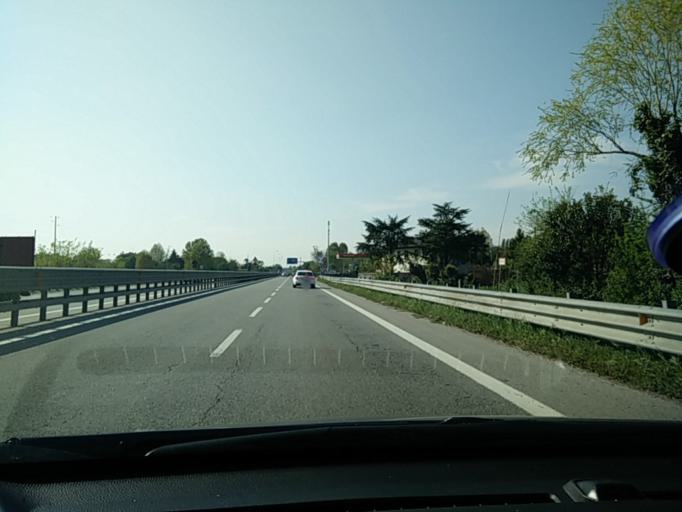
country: IT
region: Veneto
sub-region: Provincia di Venezia
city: Campalto
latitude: 45.5080
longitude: 12.2677
